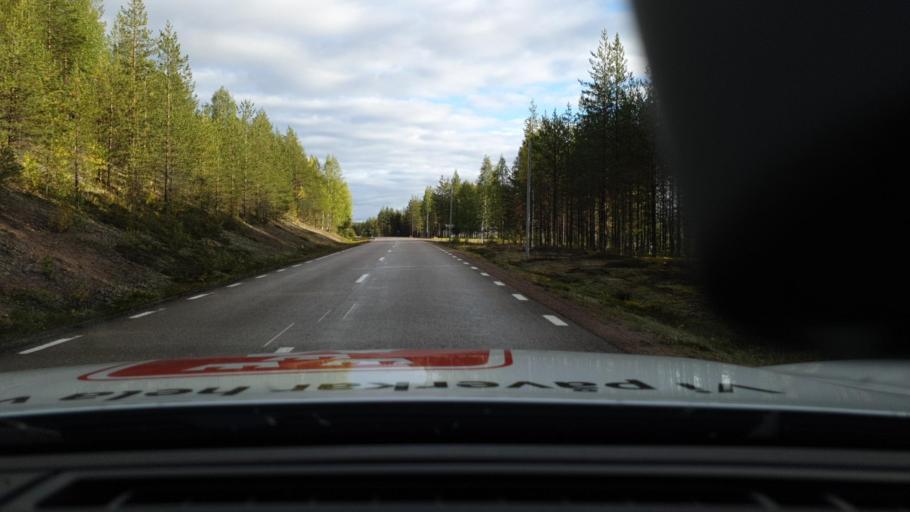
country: SE
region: Norrbotten
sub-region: Overkalix Kommun
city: OEverkalix
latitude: 66.6266
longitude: 22.7366
